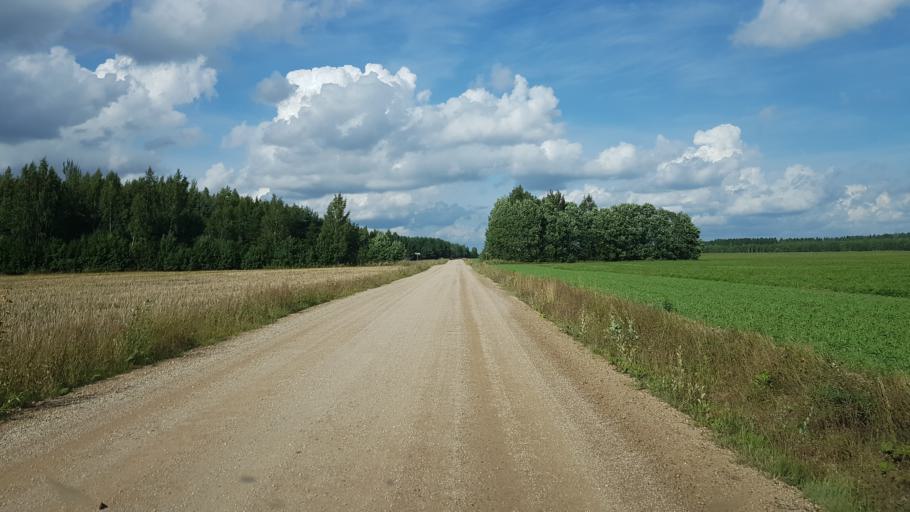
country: RU
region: Pskov
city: Pechory
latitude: 57.7802
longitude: 27.4710
